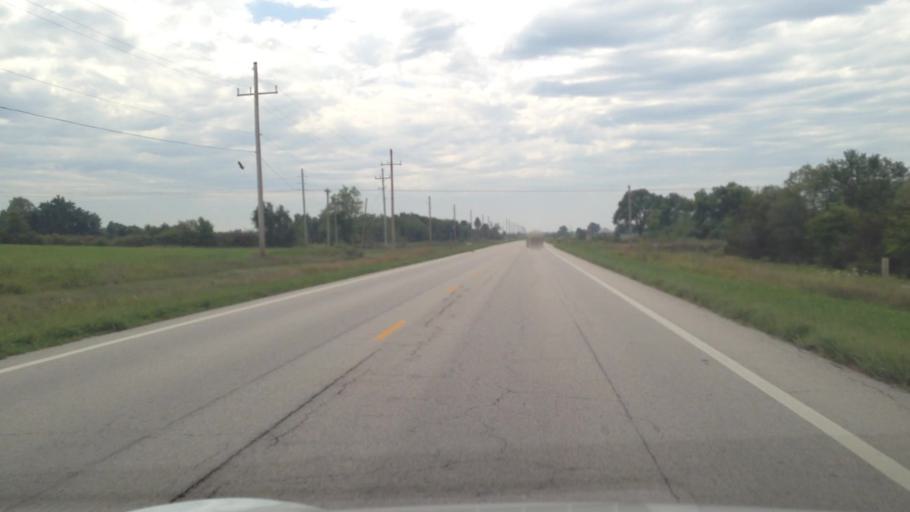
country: US
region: Kansas
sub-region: Allen County
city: Iola
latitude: 37.9520
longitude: -95.1700
